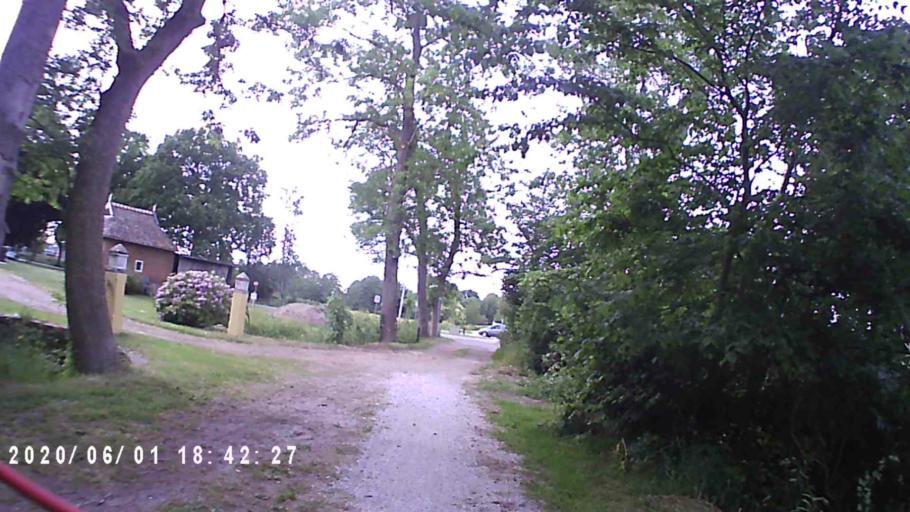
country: NL
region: Friesland
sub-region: Gemeente Tytsjerksteradiel
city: Eastermar
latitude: 53.1733
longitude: 6.0658
